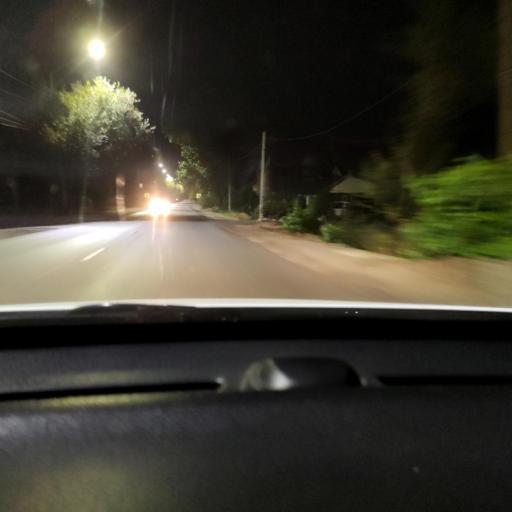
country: RU
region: Voronezj
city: Voronezh
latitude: 51.7326
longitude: 39.2622
